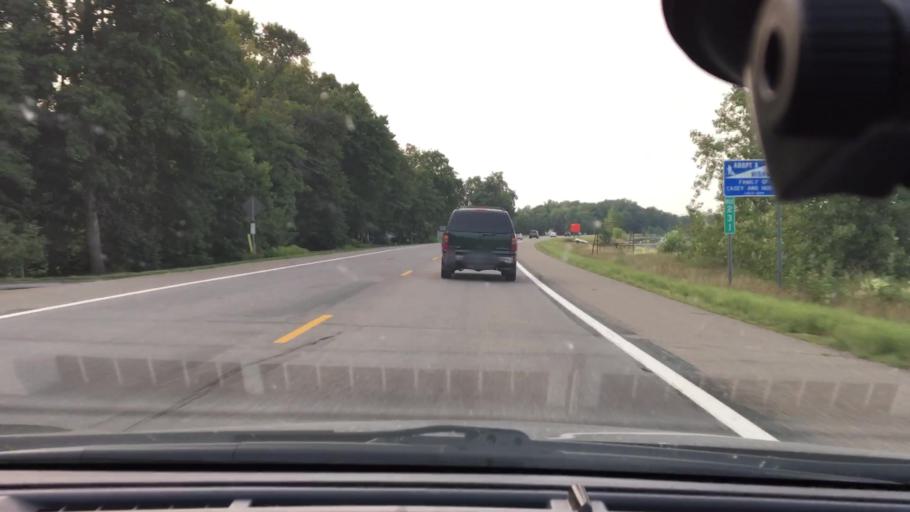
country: US
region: Minnesota
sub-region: Mille Lacs County
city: Vineland
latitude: 46.2562
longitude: -93.8223
